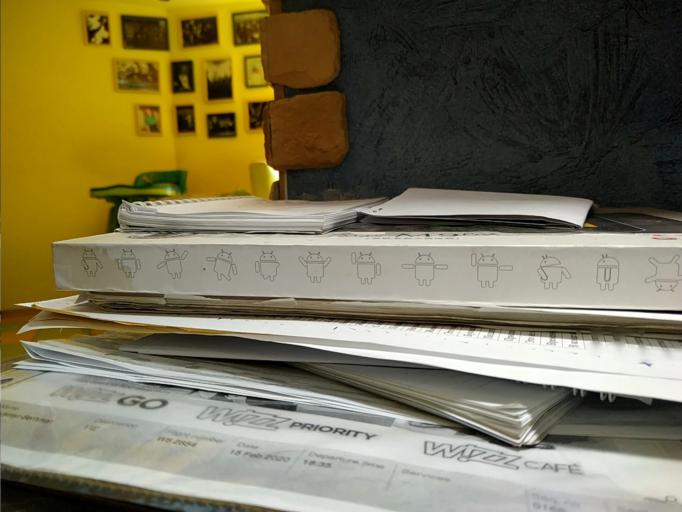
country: RU
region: Novgorod
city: Utorgosh
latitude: 58.1276
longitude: 30.0724
